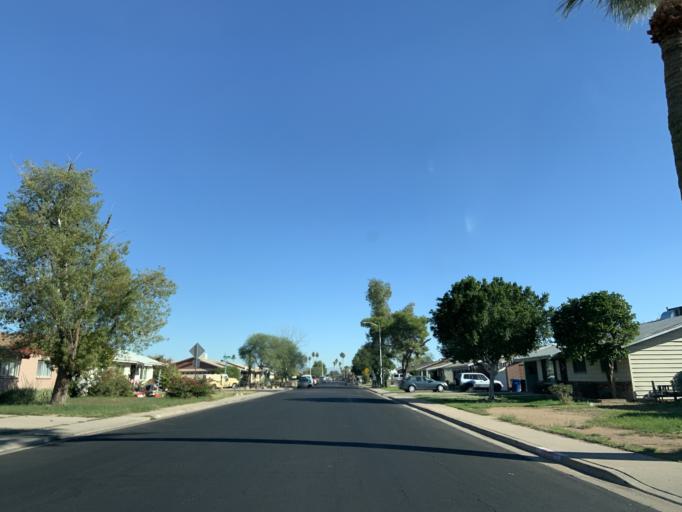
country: US
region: Arizona
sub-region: Maricopa County
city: Tempe
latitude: 33.4064
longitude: -111.8689
